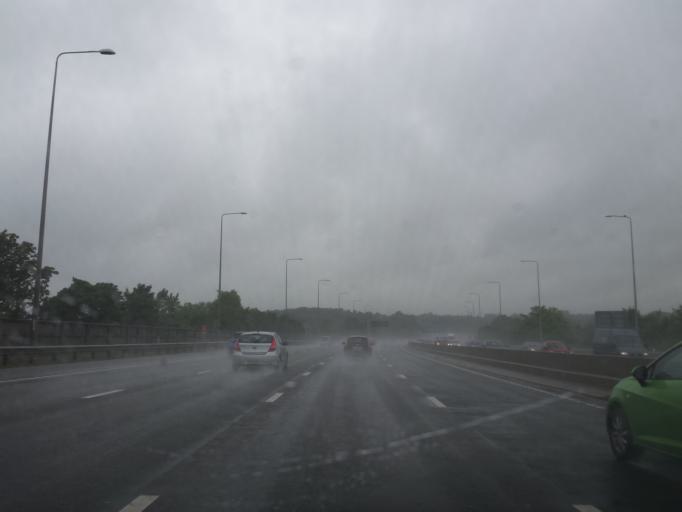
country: GB
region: England
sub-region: Derbyshire
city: Ilkeston
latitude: 52.9398
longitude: -1.2847
